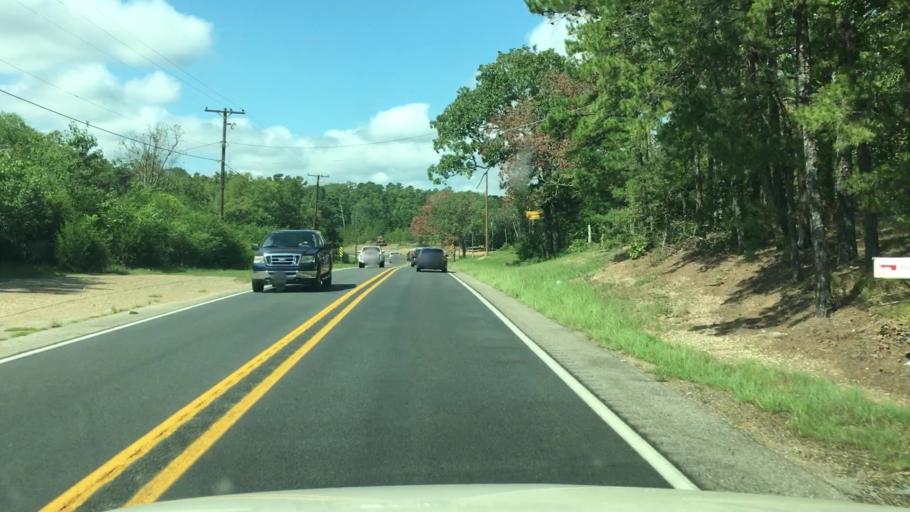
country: US
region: Arkansas
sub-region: Garland County
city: Lake Hamilton
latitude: 34.3903
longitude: -93.1186
